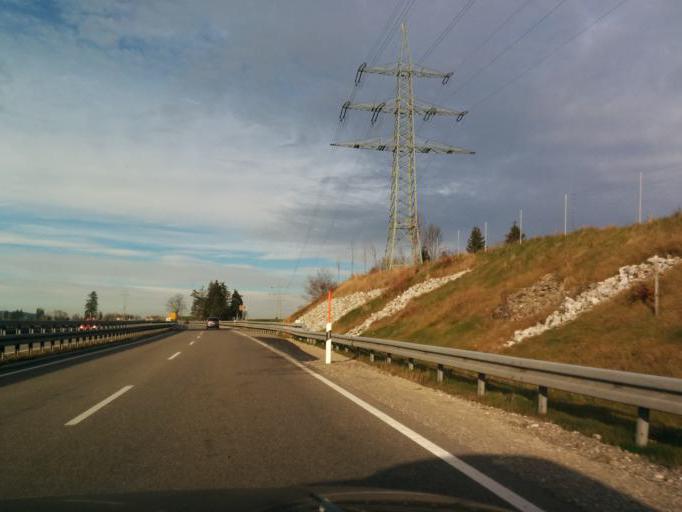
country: DE
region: Bavaria
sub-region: Swabia
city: Rettenberg
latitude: 47.6042
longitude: 10.2730
